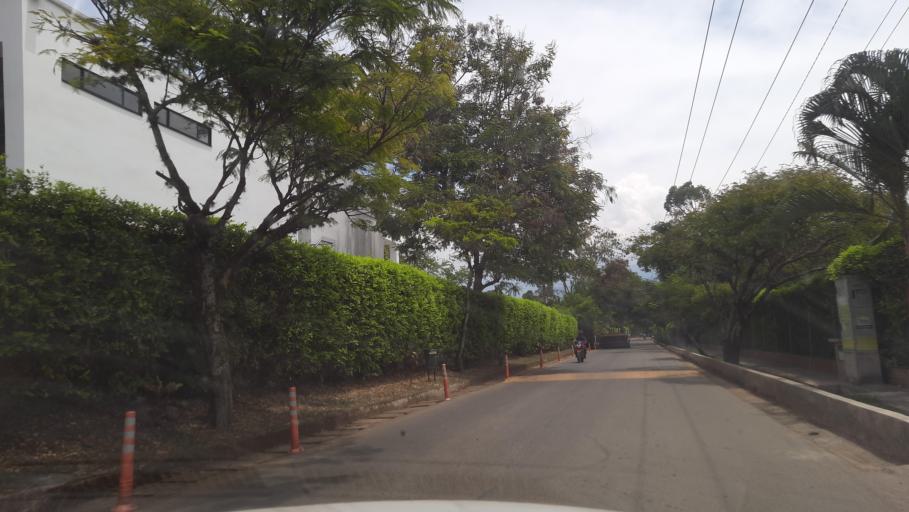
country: CO
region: Valle del Cauca
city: Jamundi
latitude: 3.2698
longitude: -76.5197
